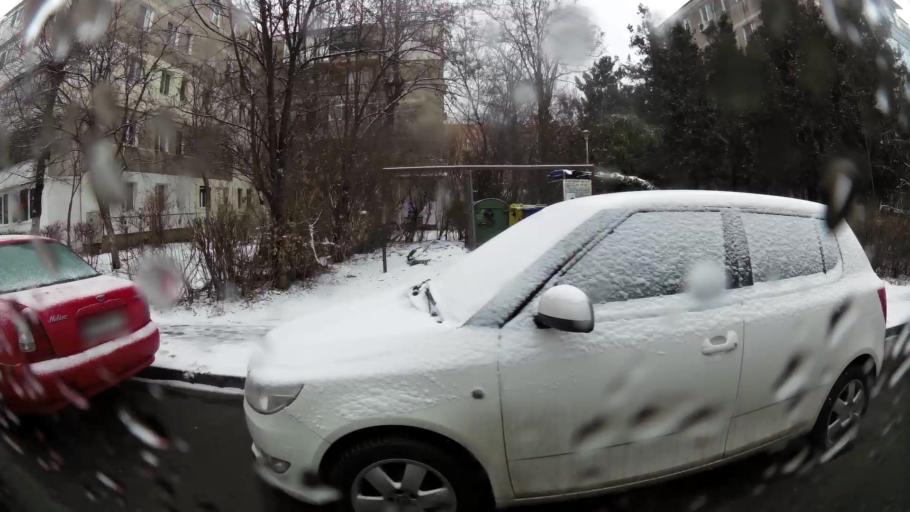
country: RO
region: Prahova
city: Ploiesti
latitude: 44.9328
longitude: 25.9864
